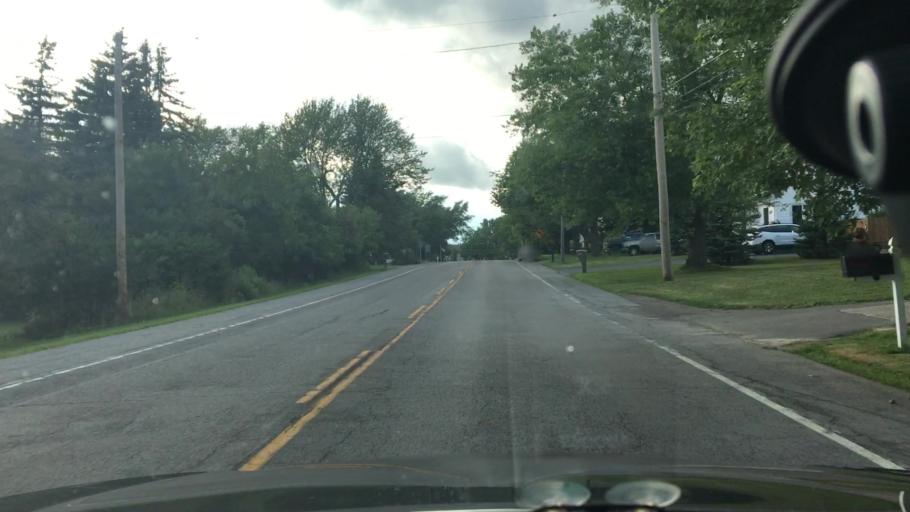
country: US
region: New York
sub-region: Erie County
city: Depew
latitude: 42.8374
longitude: -78.7167
